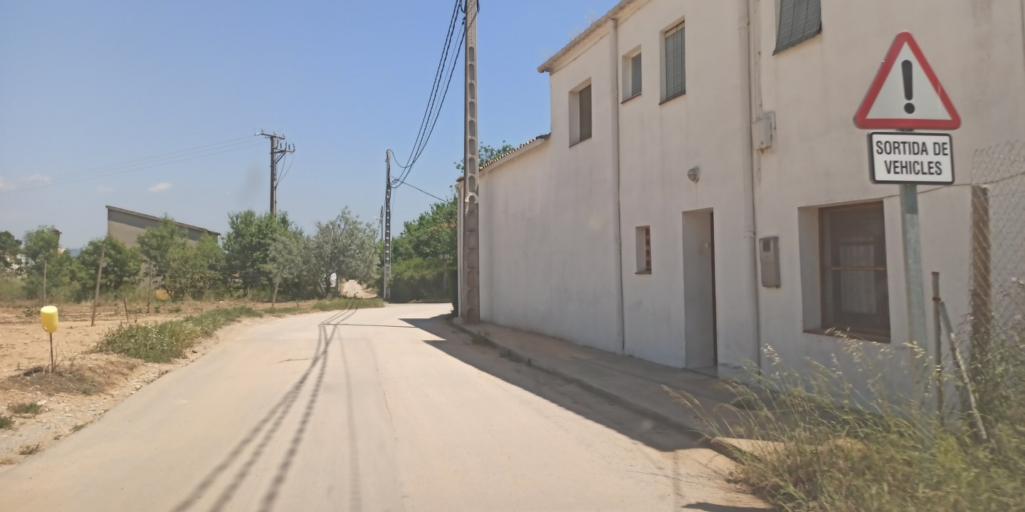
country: ES
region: Catalonia
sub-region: Provincia de Barcelona
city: Vilobi del Penedes
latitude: 41.3465
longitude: 1.6538
